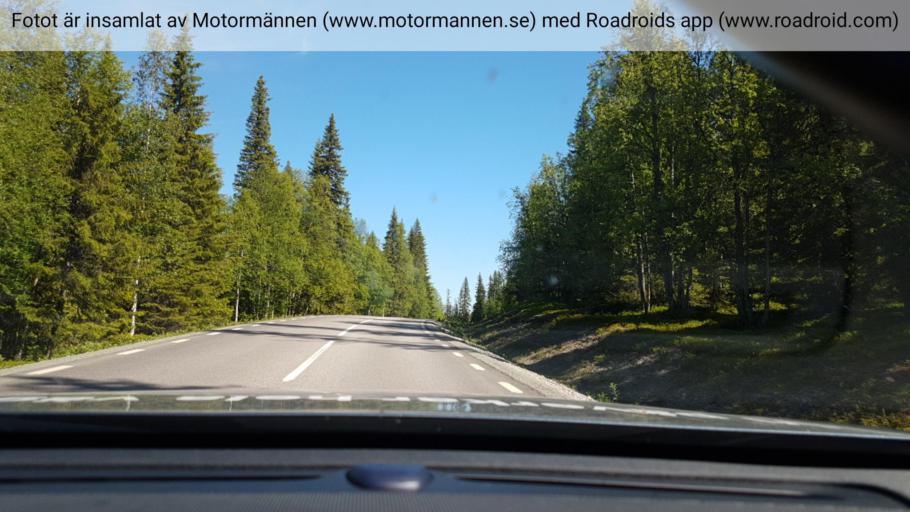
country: SE
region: Vaesterbotten
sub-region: Asele Kommun
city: Insjon
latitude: 64.7304
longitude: 17.5316
